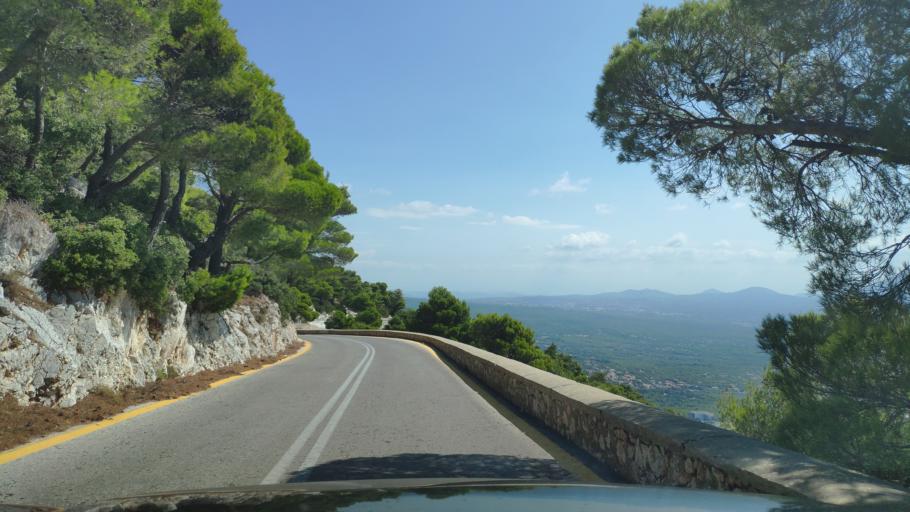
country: GR
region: Attica
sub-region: Nomarchia Anatolikis Attikis
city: Thrakomakedones
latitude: 38.1406
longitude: 23.7214
